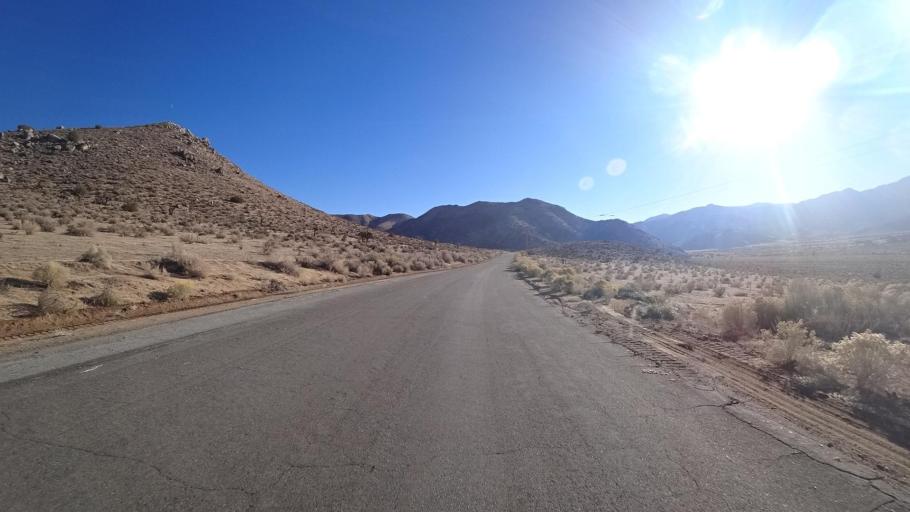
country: US
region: California
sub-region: Kern County
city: Weldon
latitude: 35.5925
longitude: -118.2400
